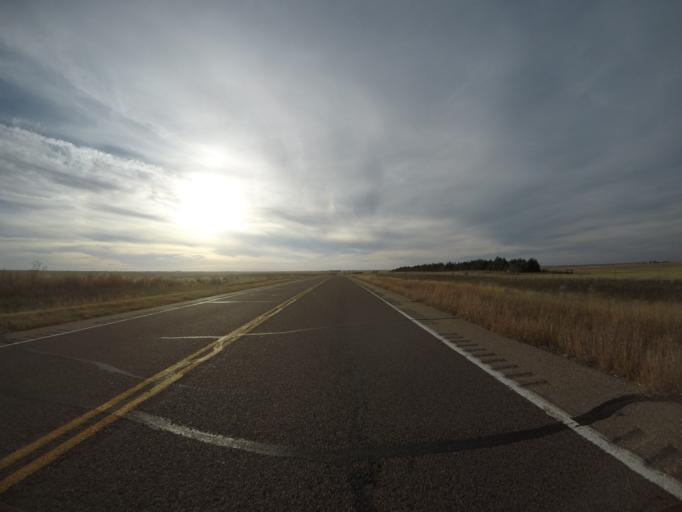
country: US
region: Colorado
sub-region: Kit Carson County
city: Burlington
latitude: 39.6580
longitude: -102.5027
